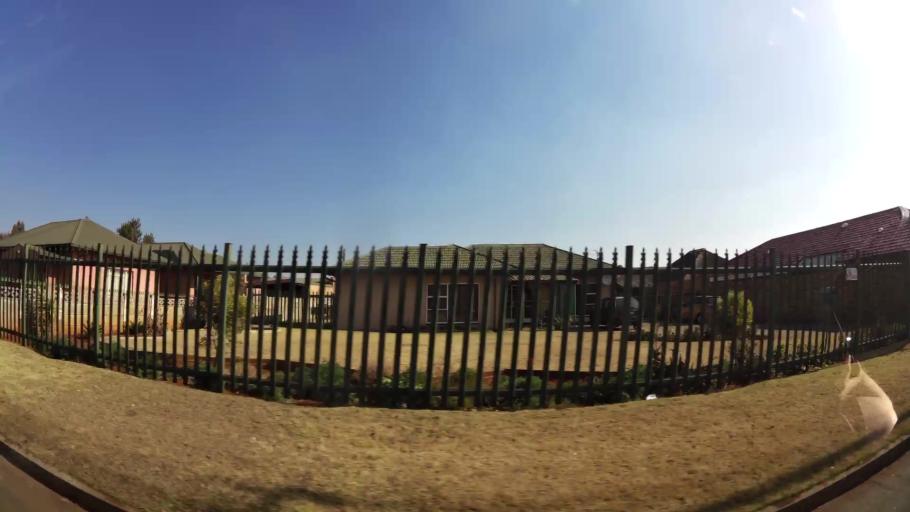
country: ZA
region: Gauteng
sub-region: West Rand District Municipality
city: Randfontein
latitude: -26.1798
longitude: 27.6942
